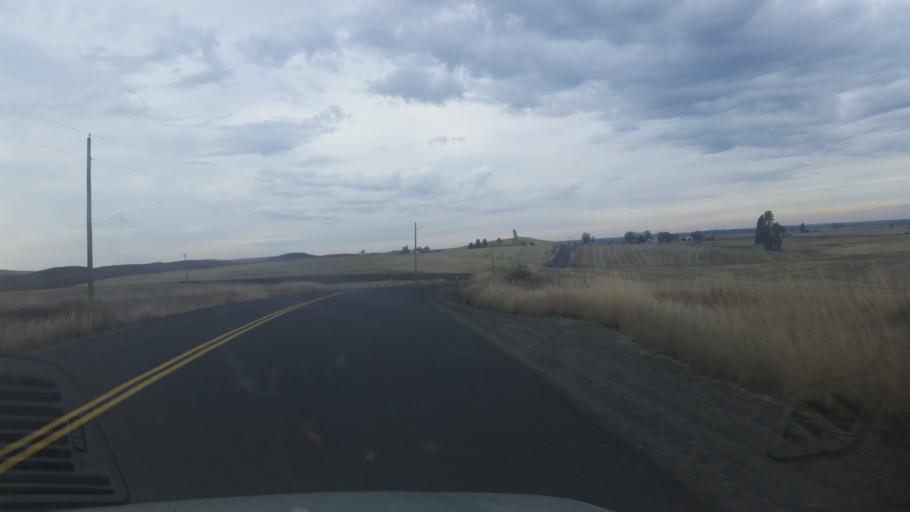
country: US
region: Washington
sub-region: Spokane County
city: Cheney
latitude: 47.3908
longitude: -117.4532
